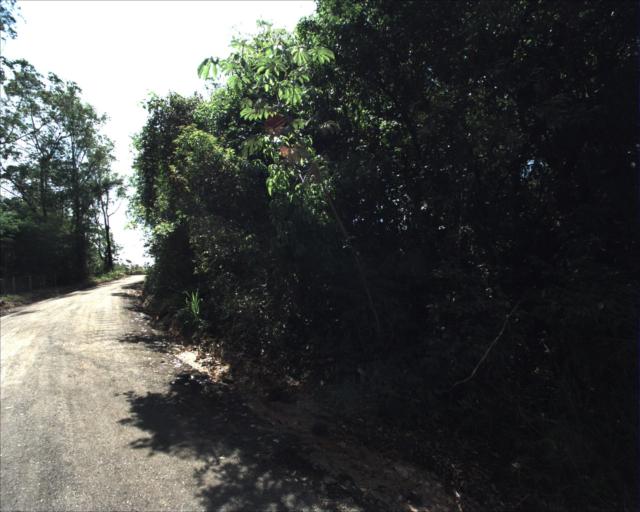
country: BR
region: Sao Paulo
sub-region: Aracoiaba Da Serra
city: Aracoiaba da Serra
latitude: -23.5552
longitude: -47.5379
